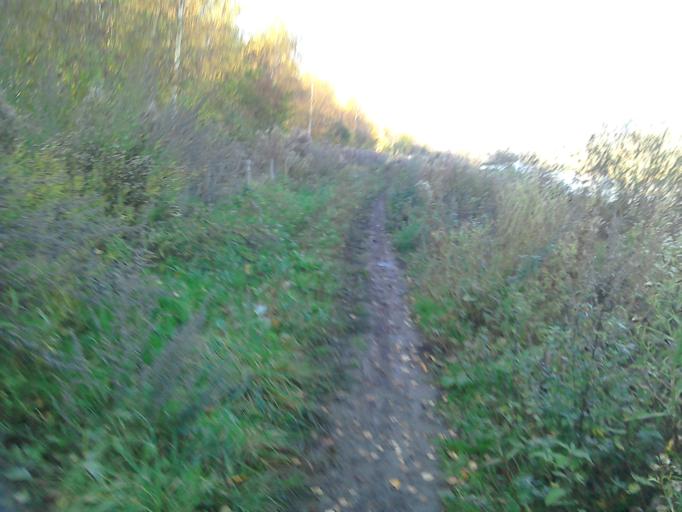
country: GB
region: England
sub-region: Oxfordshire
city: Radley
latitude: 51.6957
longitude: -1.2283
